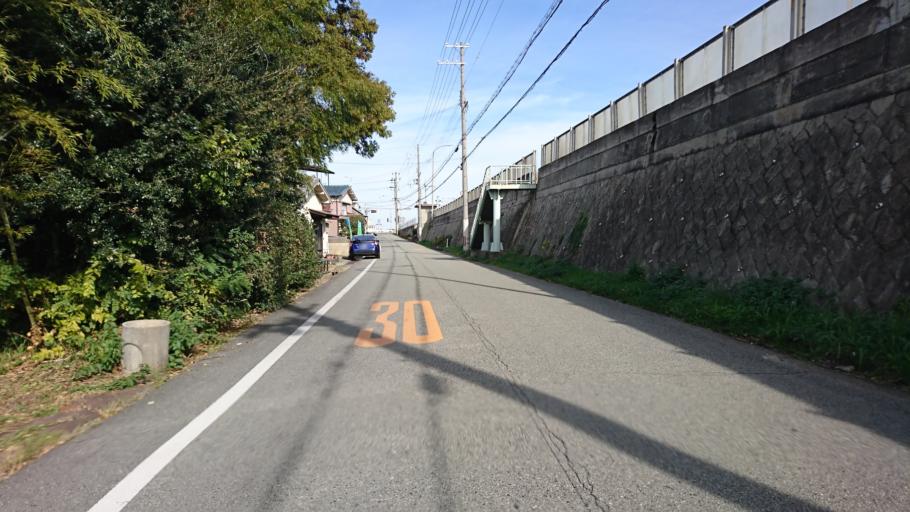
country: JP
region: Hyogo
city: Kakogawacho-honmachi
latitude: 34.7463
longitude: 134.8075
